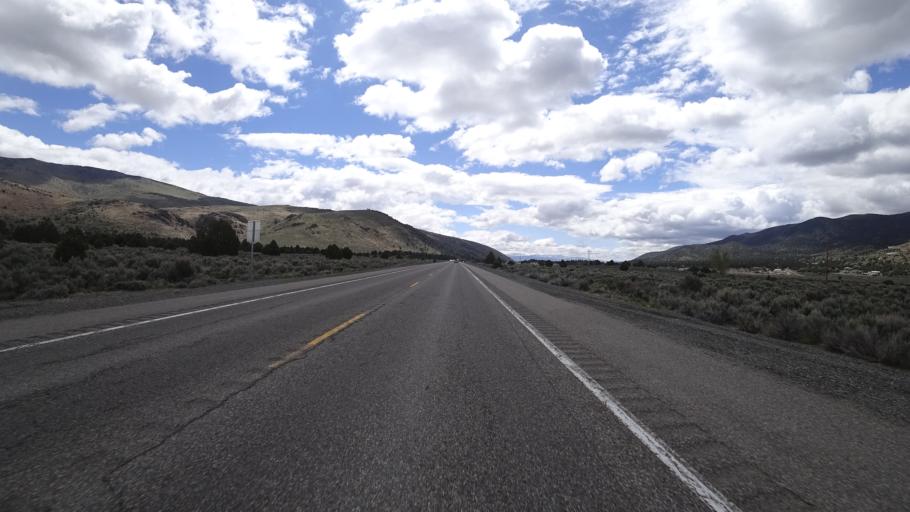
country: US
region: Nevada
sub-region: Douglas County
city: Gardnerville Ranchos
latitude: 38.7863
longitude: -119.5932
